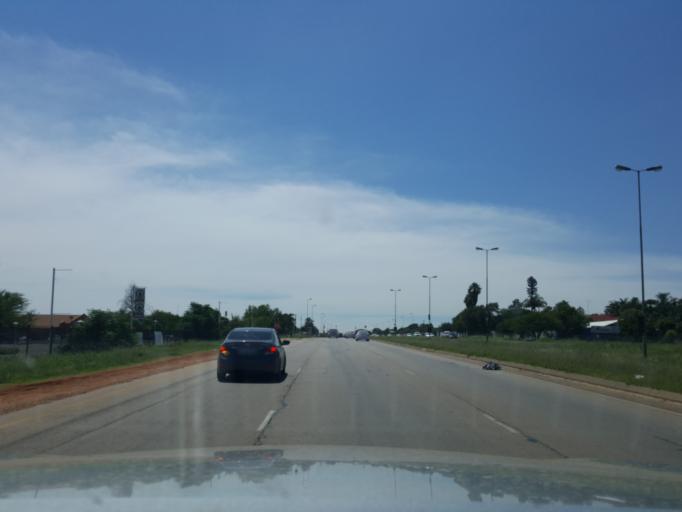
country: ZA
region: Gauteng
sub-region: City of Tshwane Metropolitan Municipality
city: Pretoria
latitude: -25.6850
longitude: 28.2950
